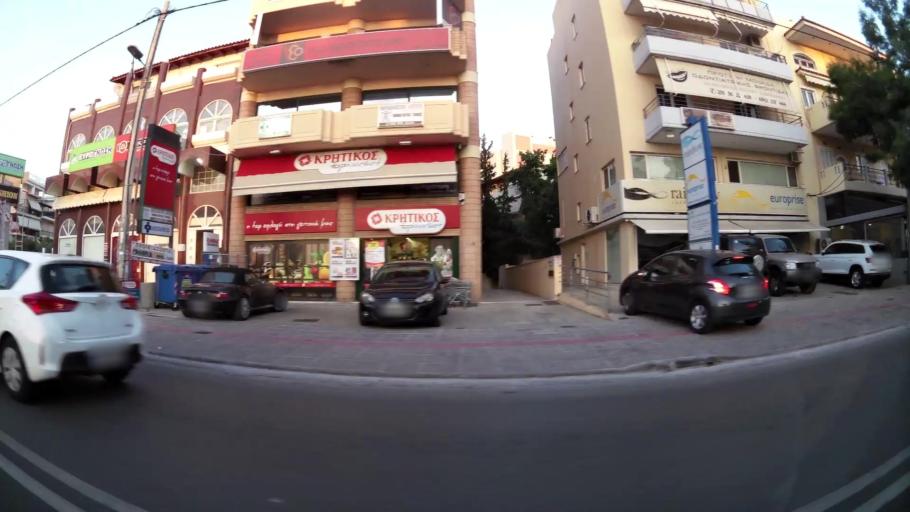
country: GR
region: Attica
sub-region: Nomarchia Athinas
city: Glyfada
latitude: 37.8817
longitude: 23.7634
